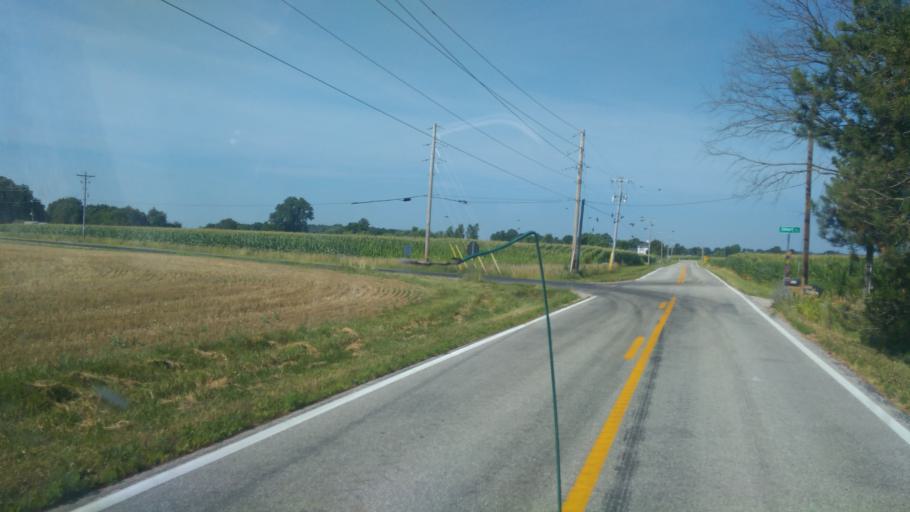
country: US
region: Ohio
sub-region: Delaware County
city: Delaware
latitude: 40.3000
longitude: -83.1907
